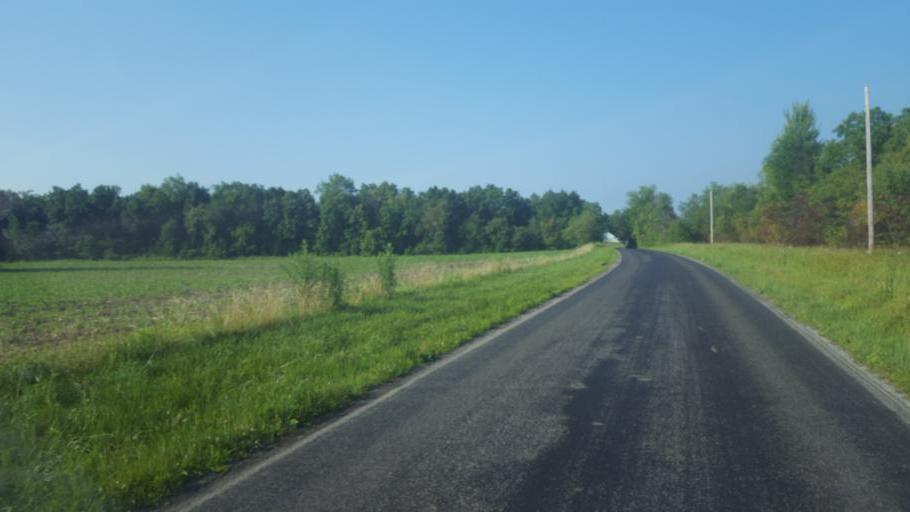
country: US
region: Ohio
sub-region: Hardin County
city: Kenton
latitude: 40.5826
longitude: -83.5722
